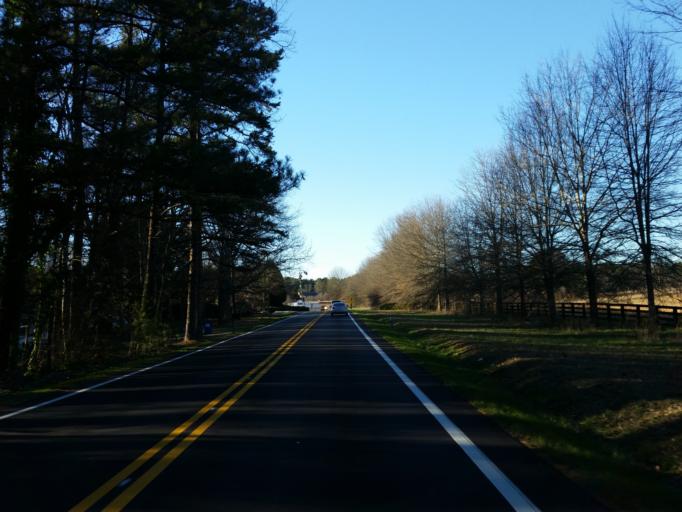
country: US
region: Georgia
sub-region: Cobb County
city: Acworth
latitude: 33.9723
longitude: -84.7137
